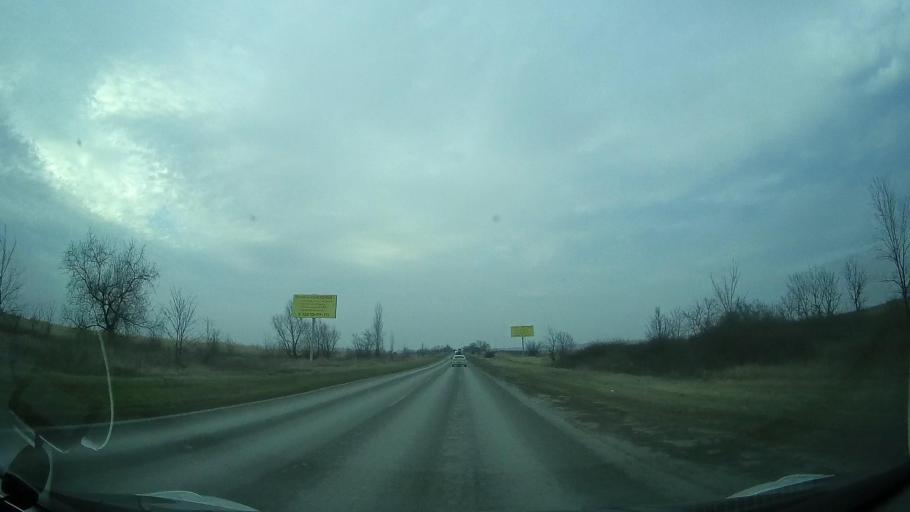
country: RU
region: Rostov
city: Ol'ginskaya
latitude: 47.2025
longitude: 39.9305
